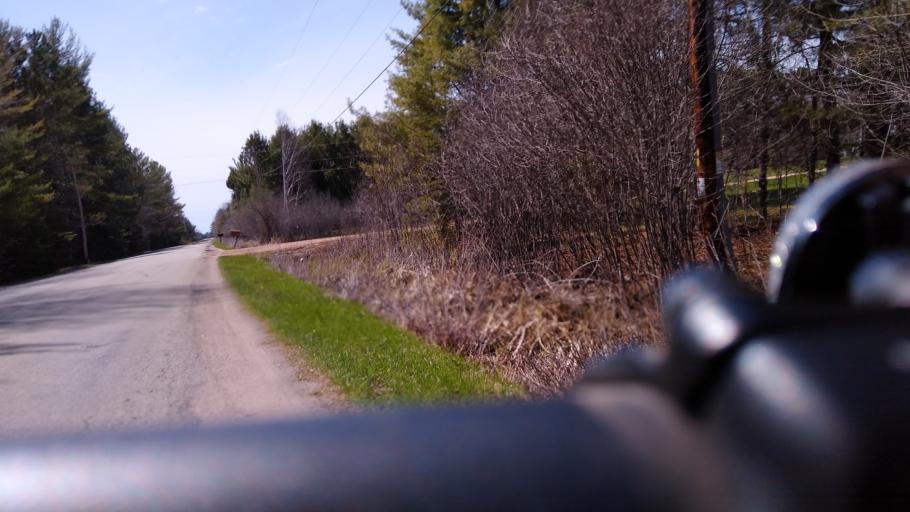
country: US
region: Michigan
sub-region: Delta County
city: Escanaba
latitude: 45.7353
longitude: -87.1686
